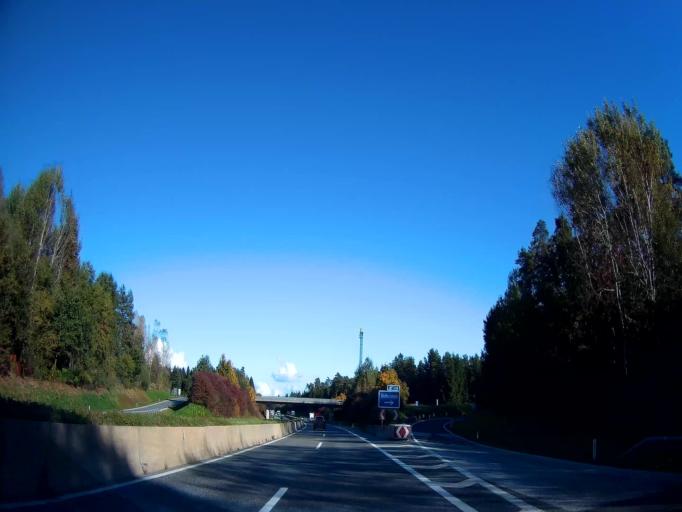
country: AT
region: Carinthia
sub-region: Politischer Bezirk Klagenfurt Land
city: Poggersdorf
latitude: 46.6380
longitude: 14.4473
